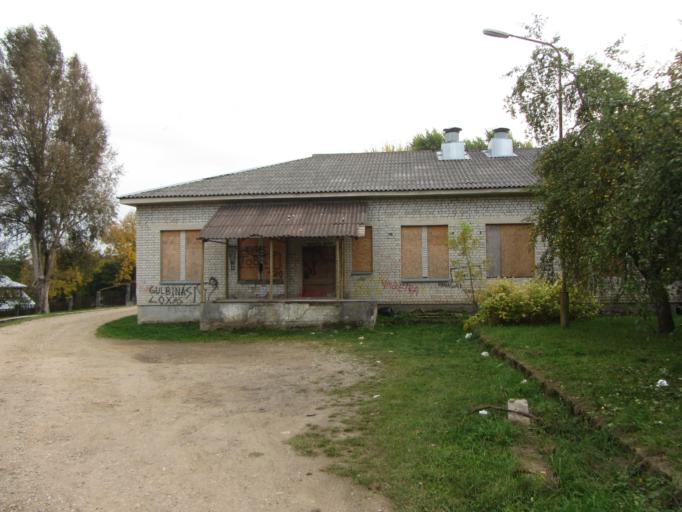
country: LT
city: Trakai
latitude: 54.6388
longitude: 24.9409
